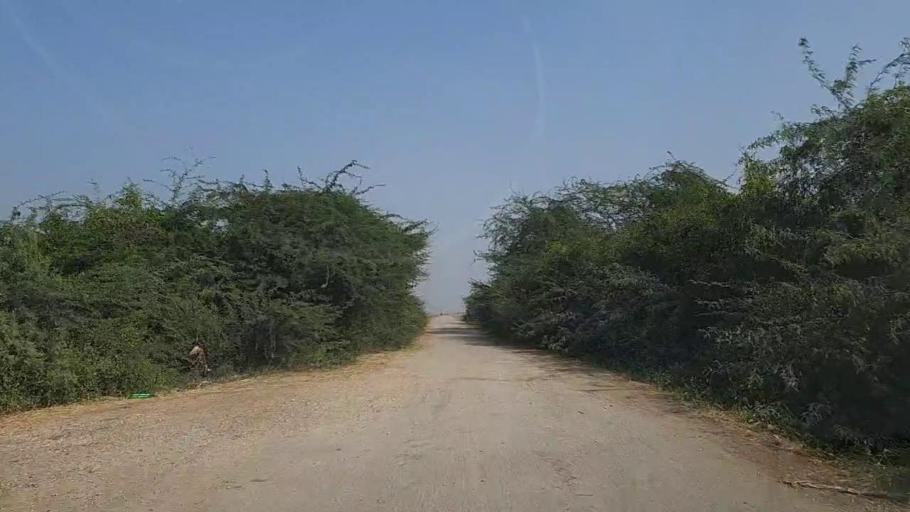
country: PK
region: Sindh
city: Keti Bandar
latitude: 24.2501
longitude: 67.7230
